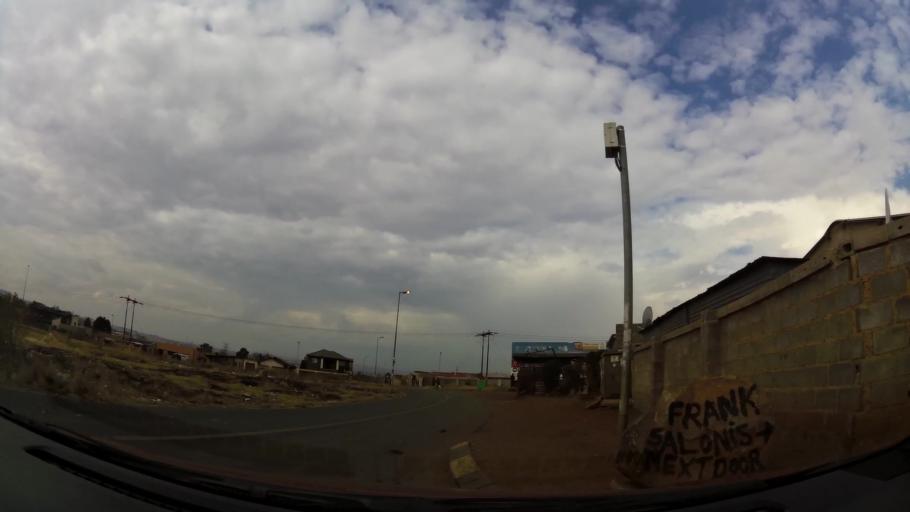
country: ZA
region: Gauteng
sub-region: City of Johannesburg Metropolitan Municipality
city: Soweto
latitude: -26.2410
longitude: 27.8581
